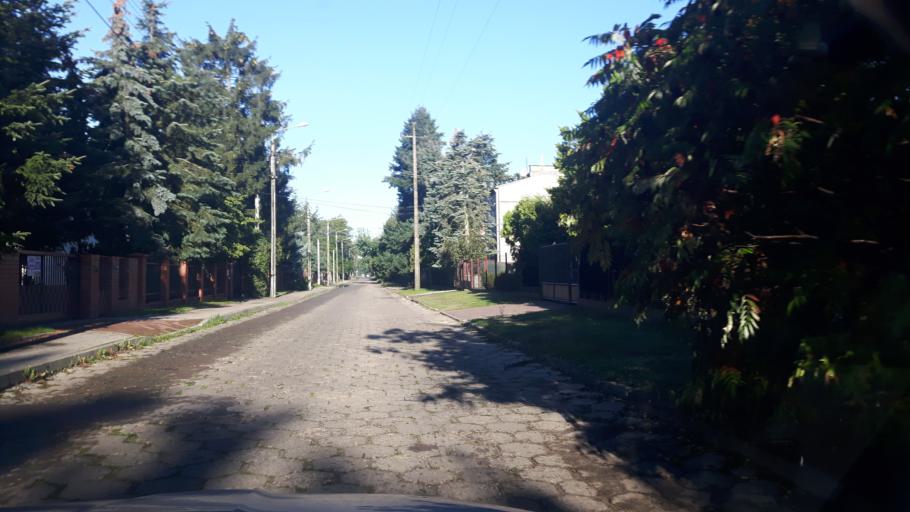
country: PL
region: Masovian Voivodeship
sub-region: Warszawa
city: Bialoleka
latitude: 52.3370
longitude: 20.9978
